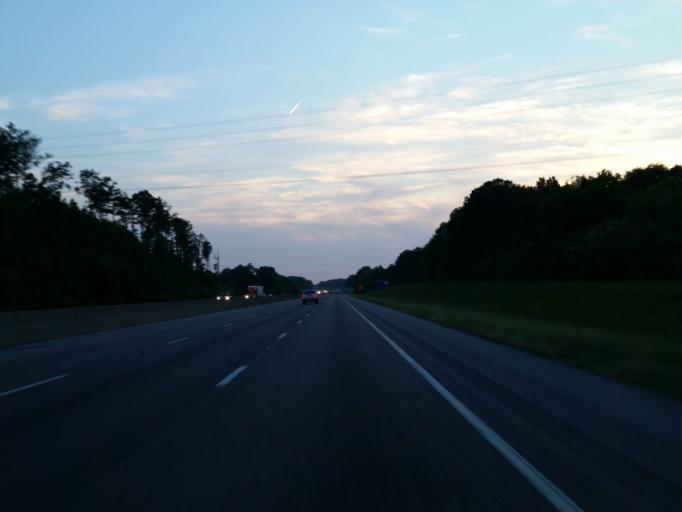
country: US
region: Alabama
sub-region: Calhoun County
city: Bynum
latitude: 33.5854
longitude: -85.9051
